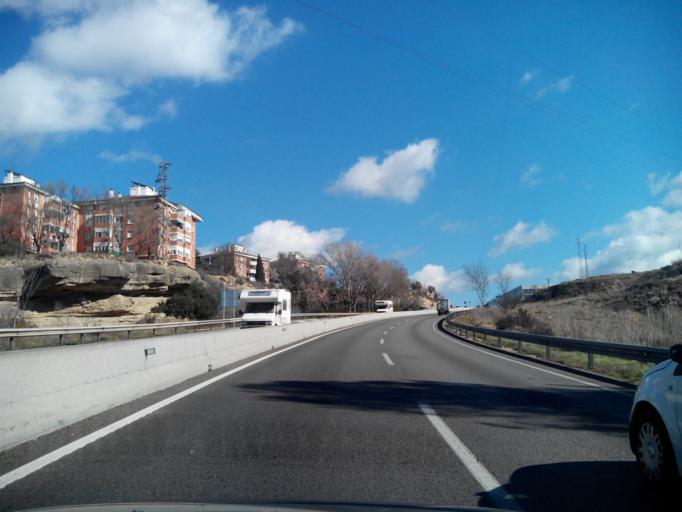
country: ES
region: Catalonia
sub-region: Provincia de Barcelona
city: Manresa
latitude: 41.7165
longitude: 1.8380
